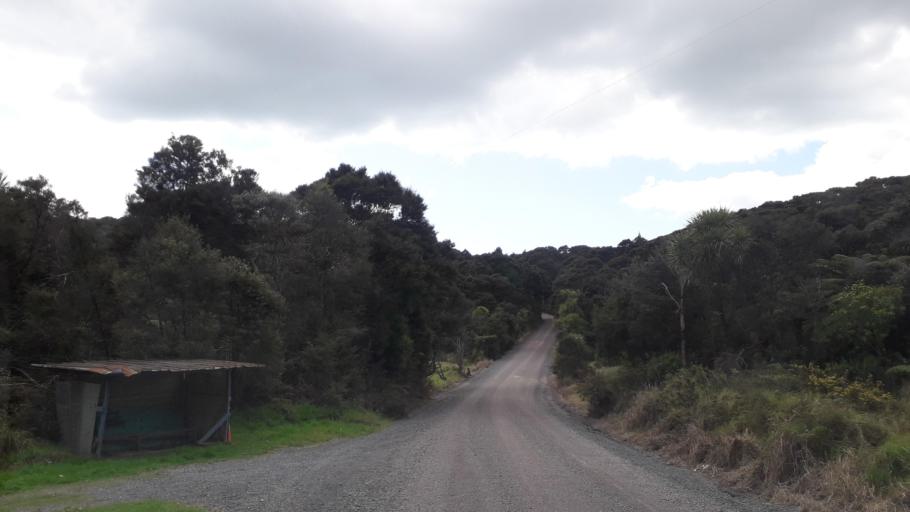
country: NZ
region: Northland
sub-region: Far North District
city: Paihia
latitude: -35.3145
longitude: 174.2243
